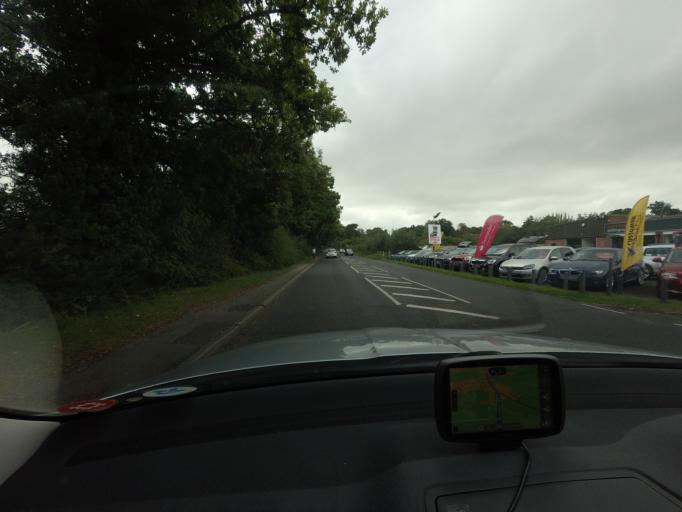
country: GB
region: England
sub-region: Kent
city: Tonbridge
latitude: 51.2198
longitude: 0.2335
